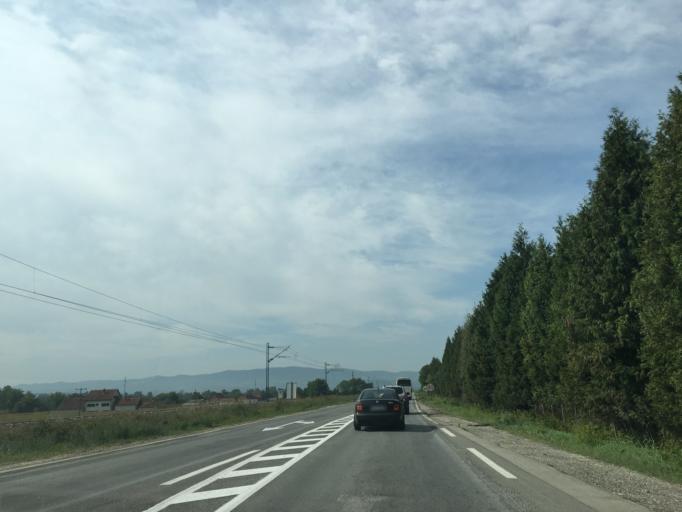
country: RS
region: Central Serbia
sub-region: Zlatiborski Okrug
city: Pozega
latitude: 43.8564
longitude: 20.0803
